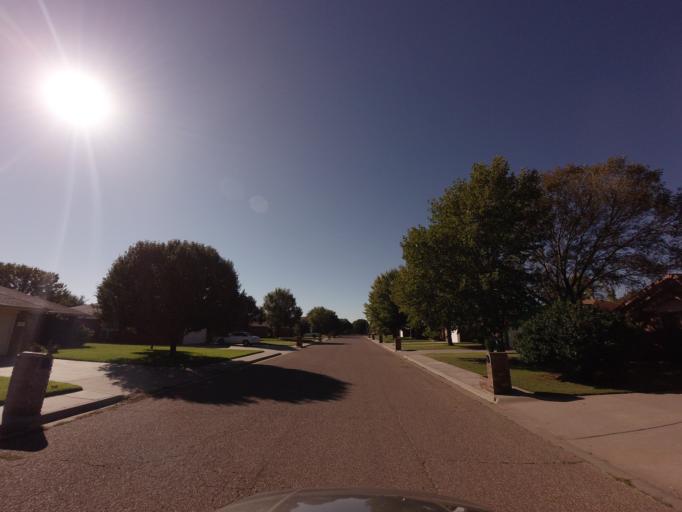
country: US
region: New Mexico
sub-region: Curry County
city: Clovis
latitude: 34.4311
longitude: -103.1768
